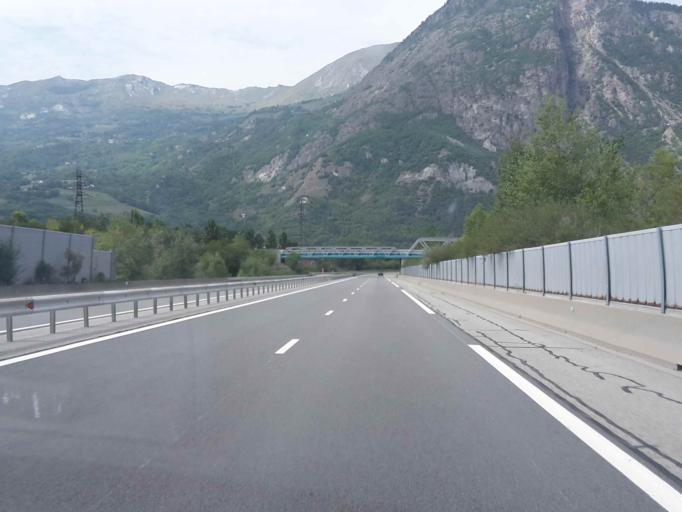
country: FR
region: Rhone-Alpes
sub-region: Departement de la Savoie
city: Villargondran
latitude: 45.2754
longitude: 6.3658
